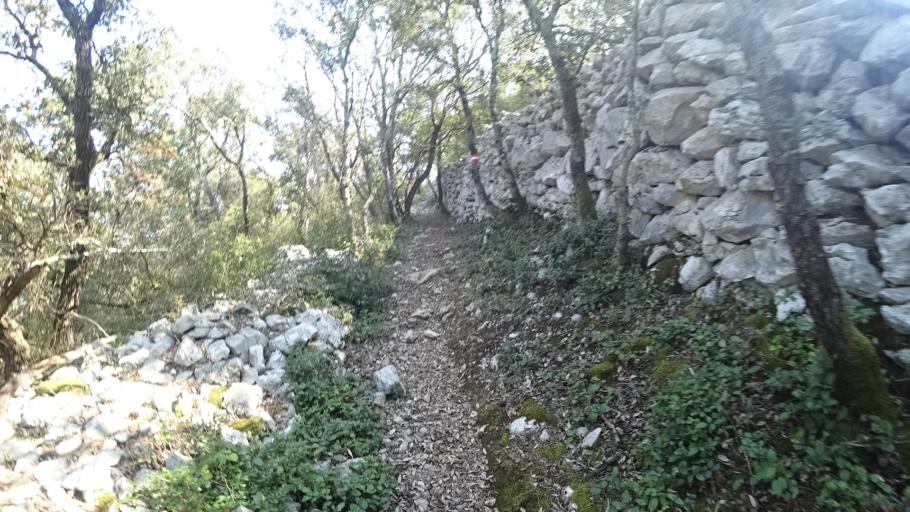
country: HR
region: Primorsko-Goranska
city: Mali Losinj
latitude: 44.4955
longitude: 14.5277
